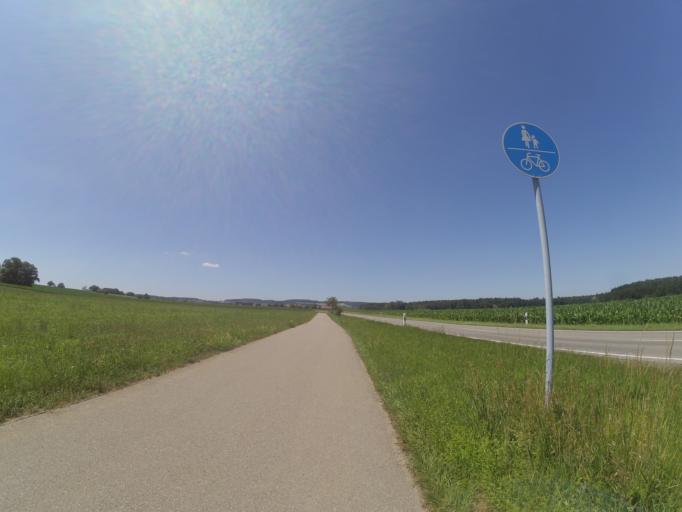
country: DE
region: Baden-Wuerttemberg
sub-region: Tuebingen Region
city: Aulendorf
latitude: 47.9338
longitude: 9.6637
